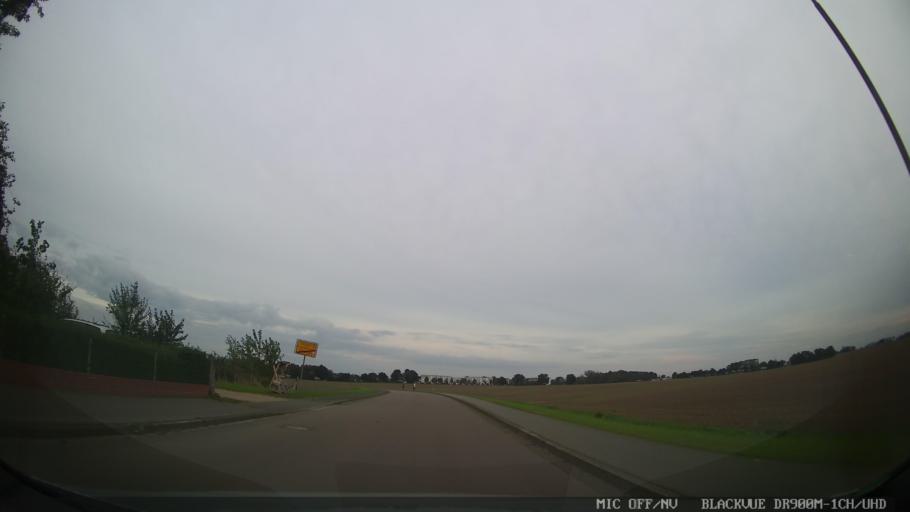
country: DE
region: Schleswig-Holstein
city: Grube
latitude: 54.2735
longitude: 11.0698
